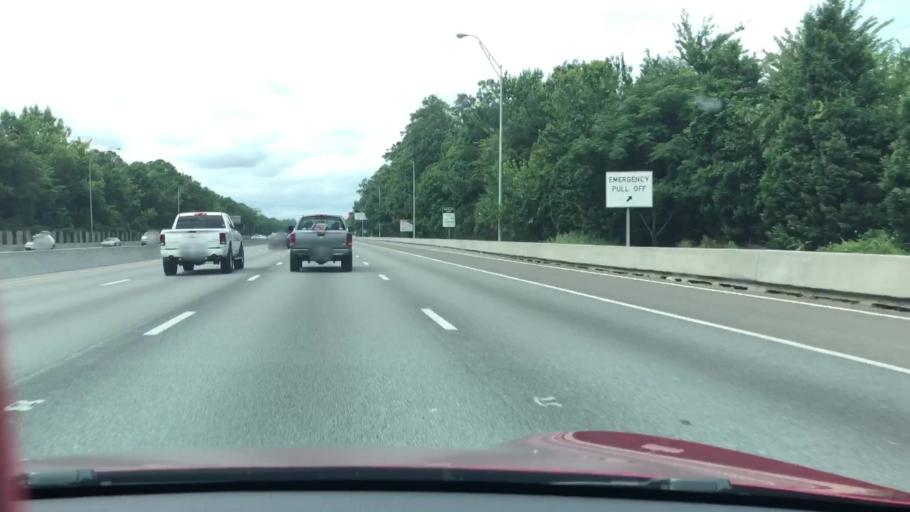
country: US
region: Virginia
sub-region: City of Virginia Beach
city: Virginia Beach
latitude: 36.8370
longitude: -76.1049
